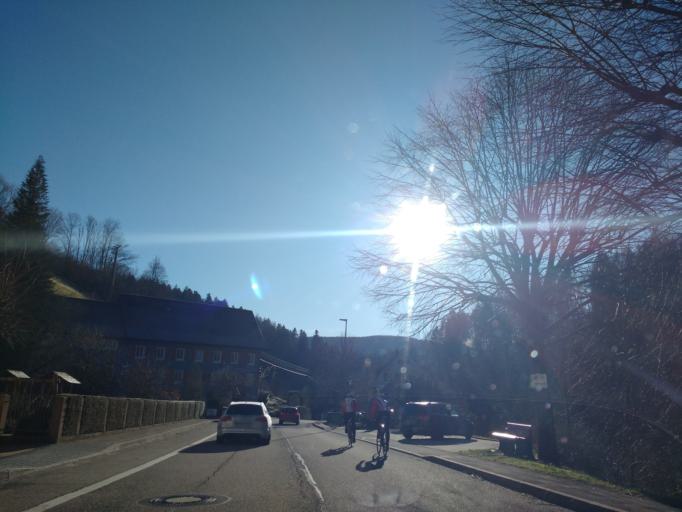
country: DE
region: Baden-Wuerttemberg
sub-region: Karlsruhe Region
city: Bad Rippoldsau-Schapbach
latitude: 48.4266
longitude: 8.3297
